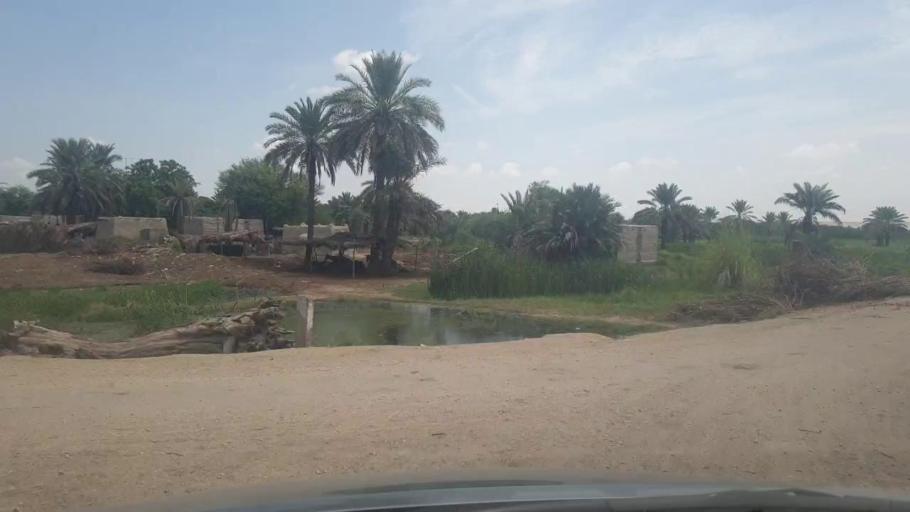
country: PK
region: Sindh
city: Kot Diji
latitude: 27.3952
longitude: 68.7605
